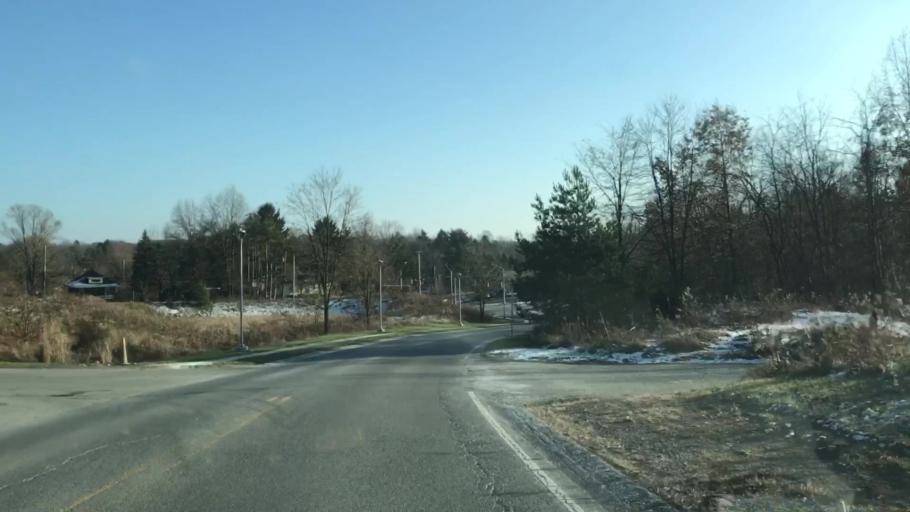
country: US
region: Pennsylvania
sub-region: Allegheny County
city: Allison Park
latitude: 40.5721
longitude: -80.0040
